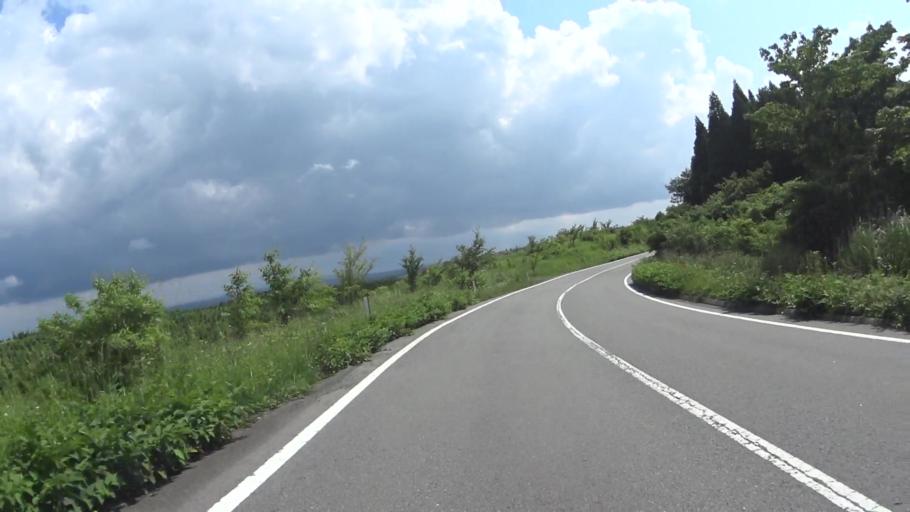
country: JP
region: Kumamoto
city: Aso
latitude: 33.0568
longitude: 131.1765
